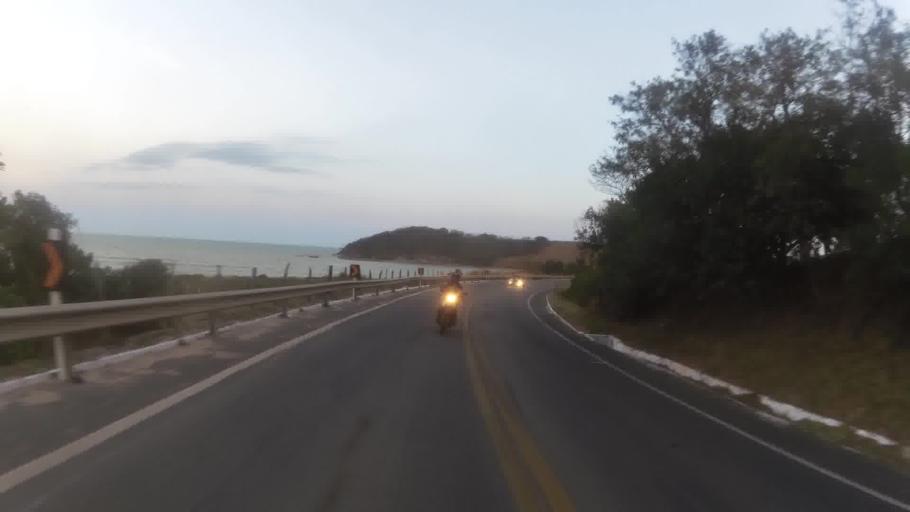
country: BR
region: Espirito Santo
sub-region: Piuma
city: Piuma
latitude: -20.8731
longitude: -40.7622
